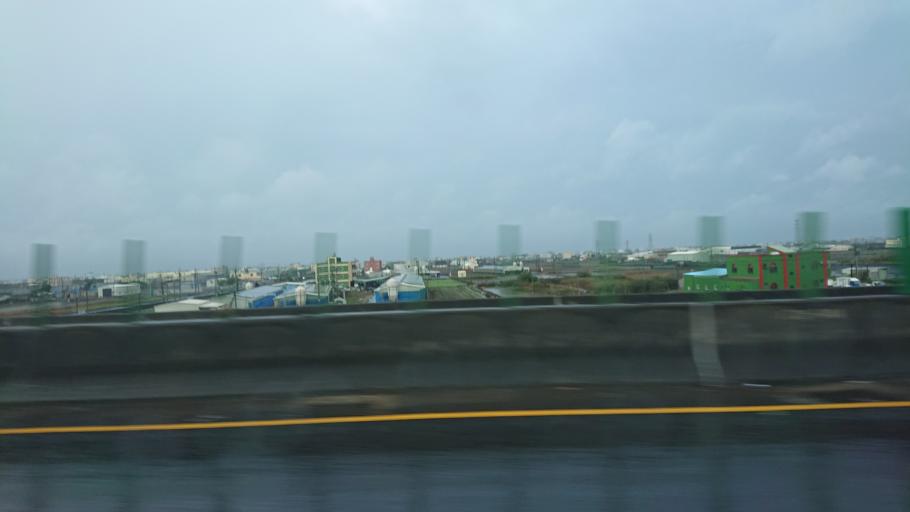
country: TW
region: Taiwan
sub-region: Changhua
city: Chang-hua
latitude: 24.1327
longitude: 120.4400
